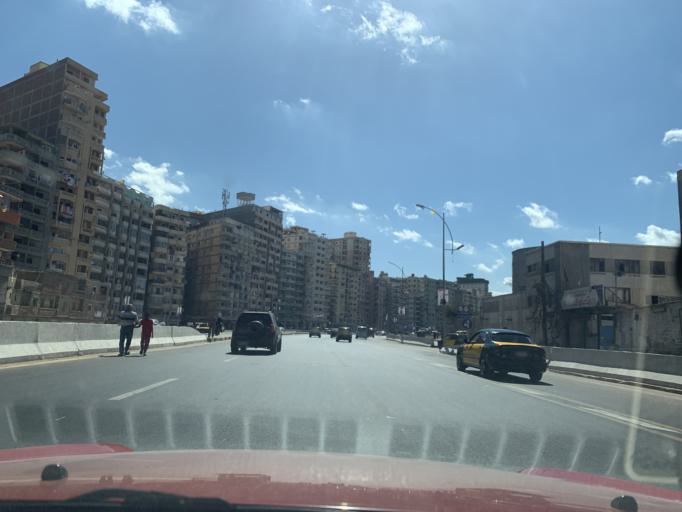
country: EG
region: Alexandria
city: Alexandria
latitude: 31.1988
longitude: 29.9355
